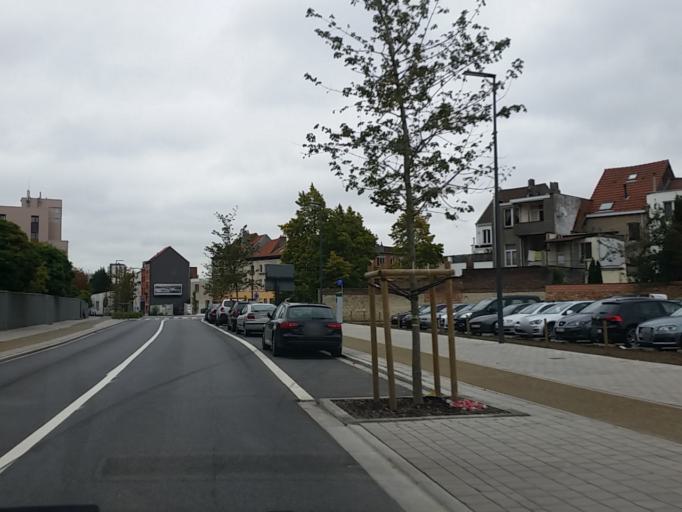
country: BE
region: Flanders
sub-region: Provincie Vlaams-Brabant
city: Drogenbos
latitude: 50.8138
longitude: 4.3178
